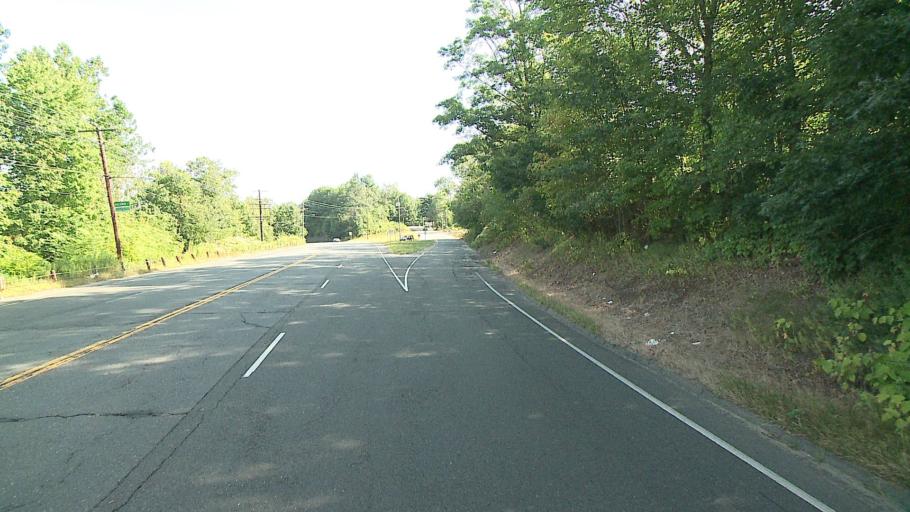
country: US
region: Connecticut
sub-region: New Haven County
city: Naugatuck
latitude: 41.5216
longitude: -73.0416
